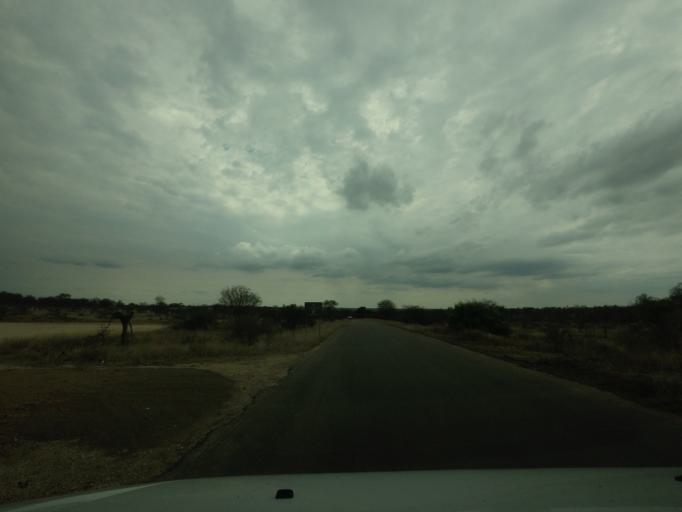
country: ZA
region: Limpopo
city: Thulamahashi
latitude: -24.4809
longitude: 31.3906
